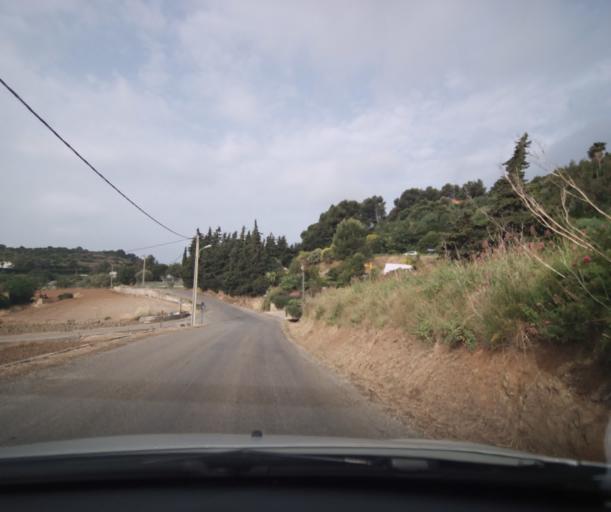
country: FR
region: Provence-Alpes-Cote d'Azur
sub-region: Departement du Var
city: Carqueiranne
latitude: 43.0873
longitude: 6.0546
